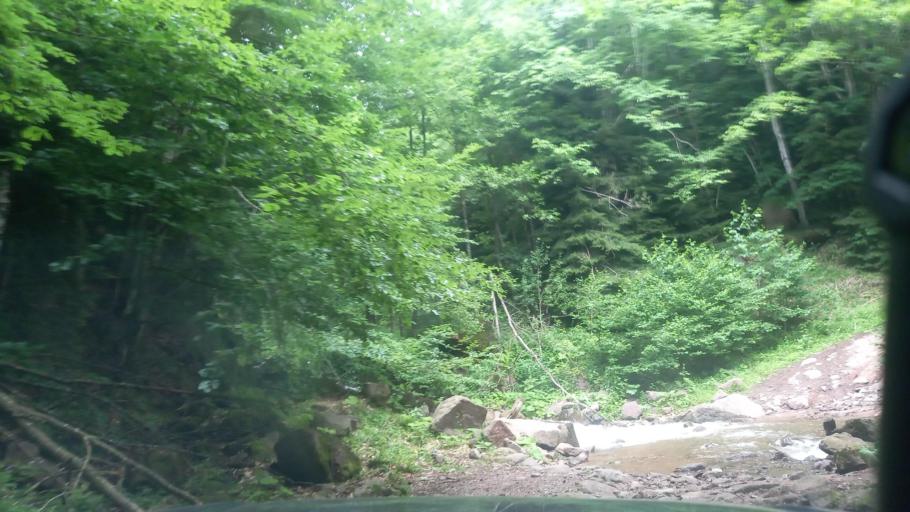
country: RU
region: Karachayevo-Cherkesiya
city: Kurdzhinovo
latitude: 43.8138
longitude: 40.8802
